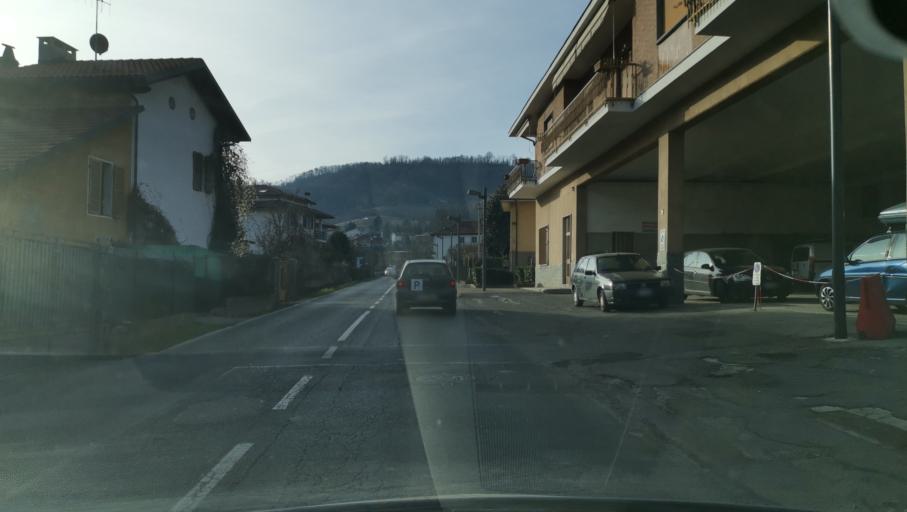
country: IT
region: Piedmont
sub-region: Provincia di Torino
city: Castiglione Torinese
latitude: 45.1090
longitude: 7.8164
